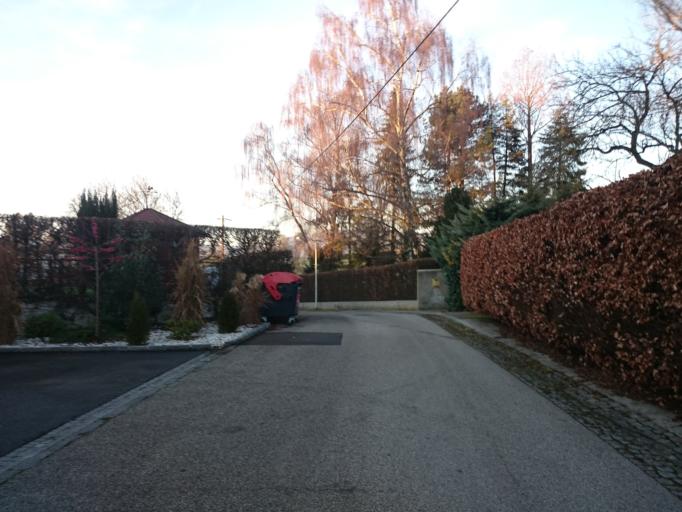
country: AT
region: Upper Austria
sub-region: Politischer Bezirk Linz-Land
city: Leonding
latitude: 48.2961
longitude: 14.2607
